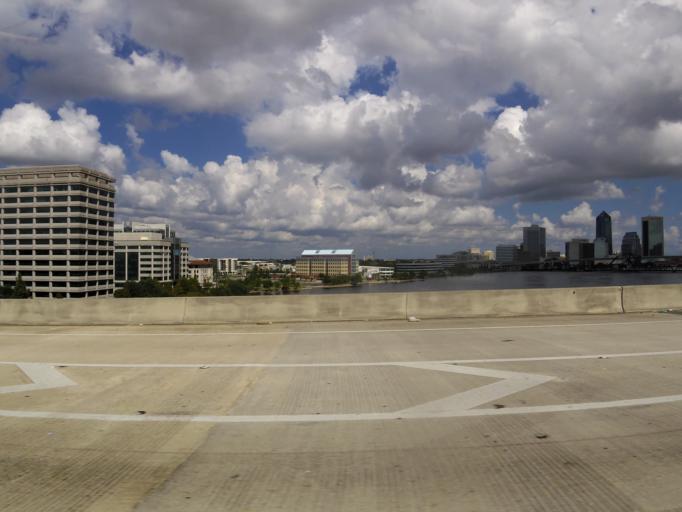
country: US
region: Florida
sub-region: Duval County
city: Jacksonville
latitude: 30.3156
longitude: -81.6743
